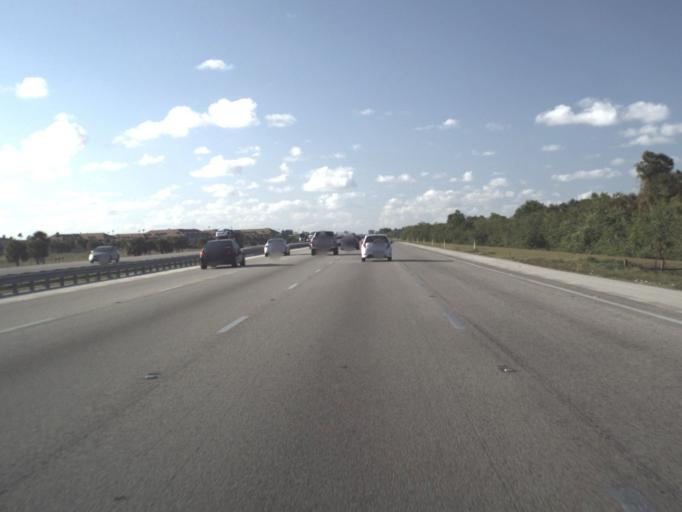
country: US
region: Florida
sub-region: Brevard County
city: Rockledge
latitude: 28.2390
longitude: -80.7208
